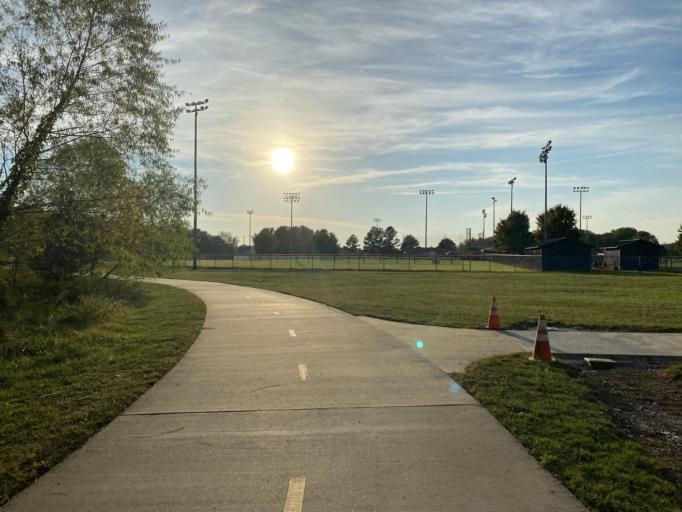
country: US
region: Arkansas
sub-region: Washington County
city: Johnson
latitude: 36.1032
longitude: -94.2045
